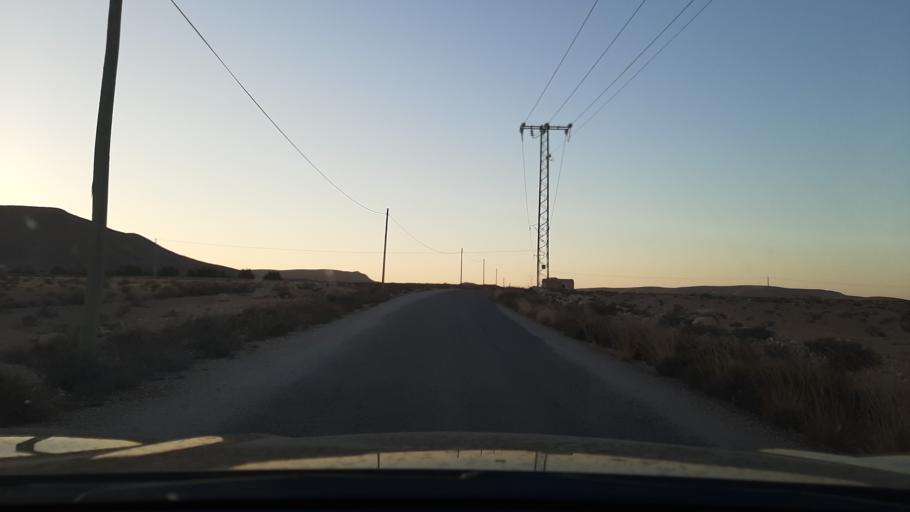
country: TN
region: Qabis
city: Matmata
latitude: 33.5493
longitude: 10.1893
